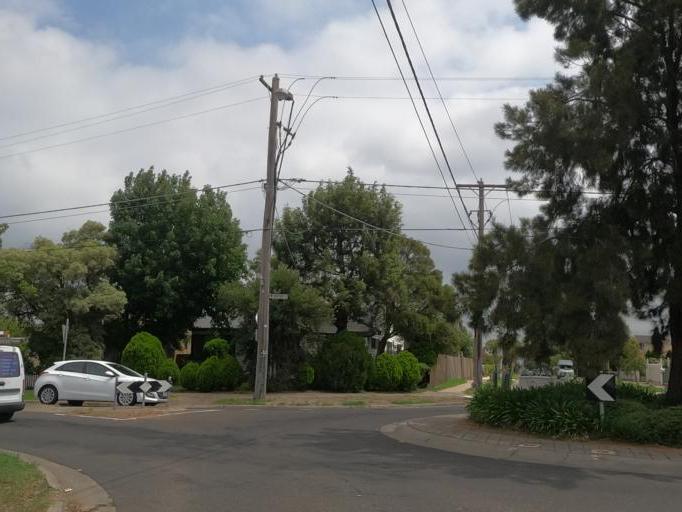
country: AU
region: Victoria
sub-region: Moreland
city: Glenroy
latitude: -37.7002
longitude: 144.9243
